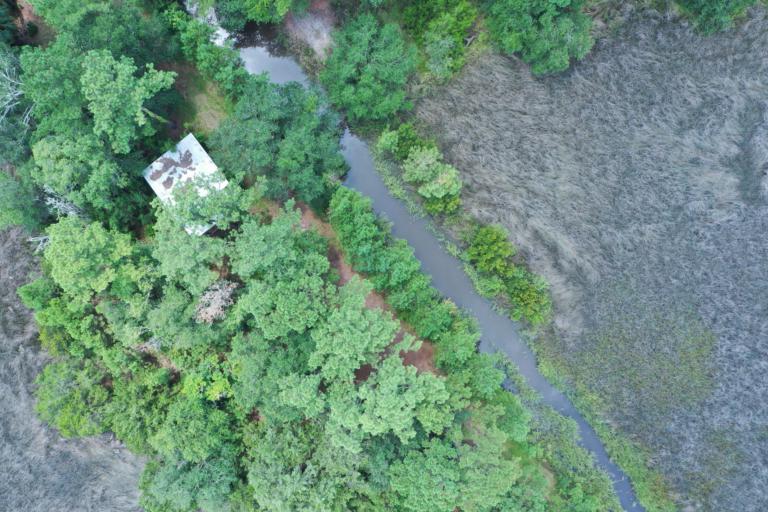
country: US
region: Georgia
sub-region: Chatham County
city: Georgetown
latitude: 32.0255
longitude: -81.2062
